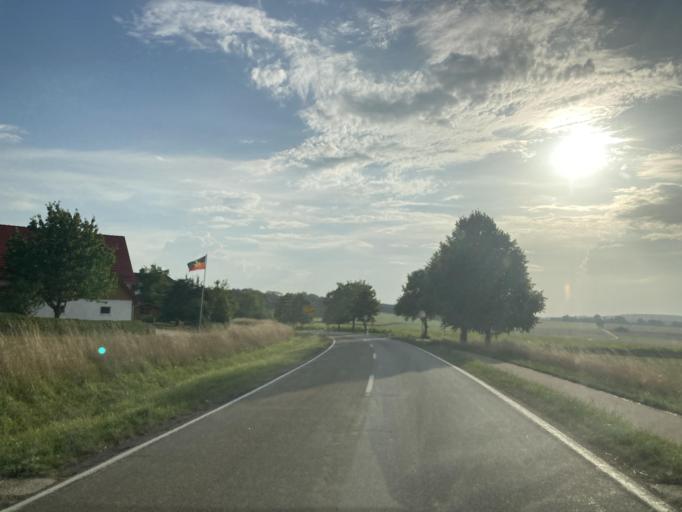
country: DE
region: Bavaria
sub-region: Swabia
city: Forheim
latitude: 48.7549
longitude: 10.4071
